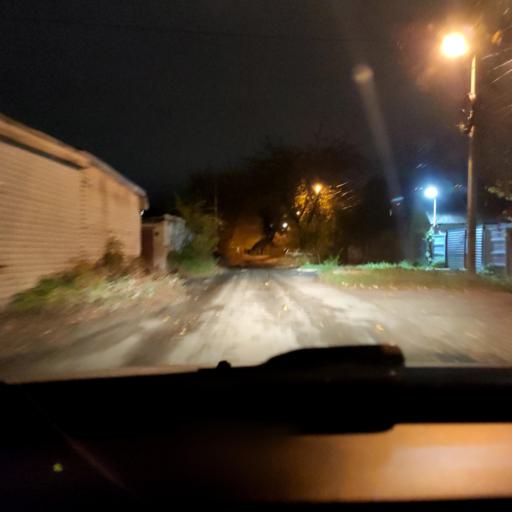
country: RU
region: Voronezj
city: Voronezh
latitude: 51.6754
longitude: 39.1970
